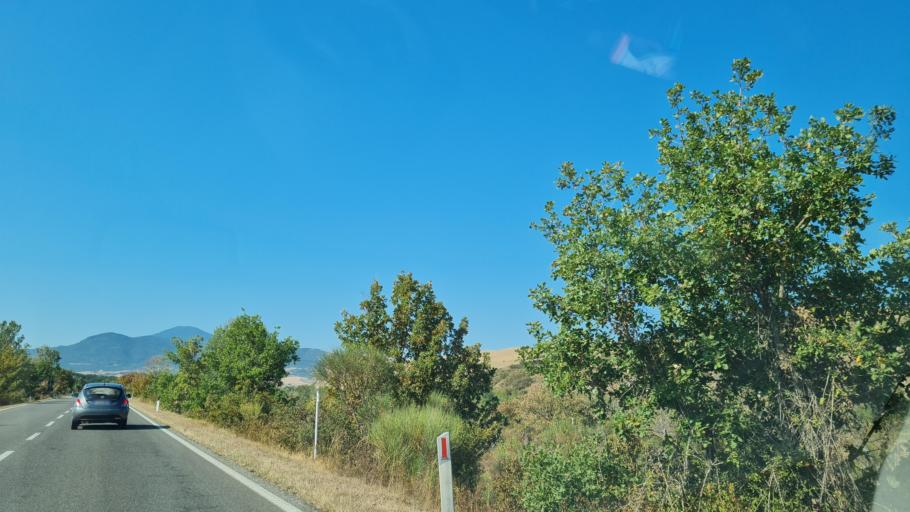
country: IT
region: Tuscany
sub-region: Provincia di Siena
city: Pienza
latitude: 43.0004
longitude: 11.7273
